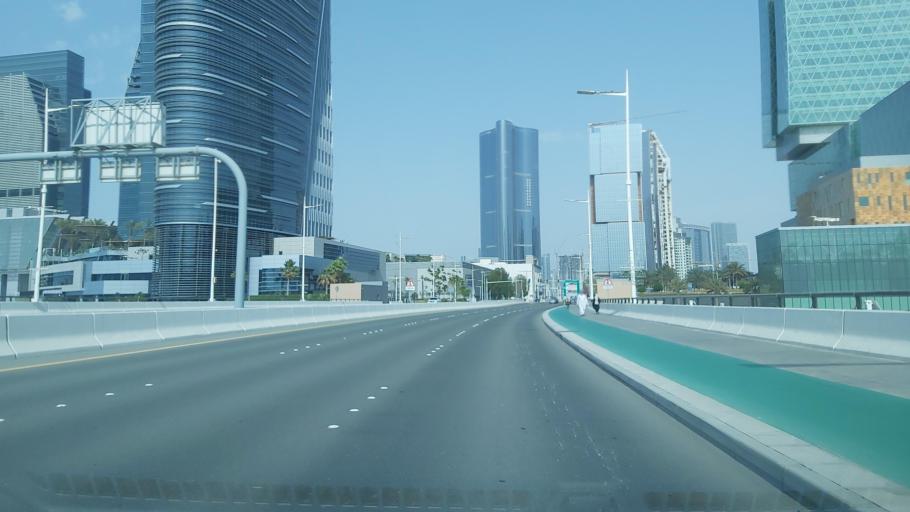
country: AE
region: Abu Dhabi
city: Abu Dhabi
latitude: 24.4991
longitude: 54.3855
